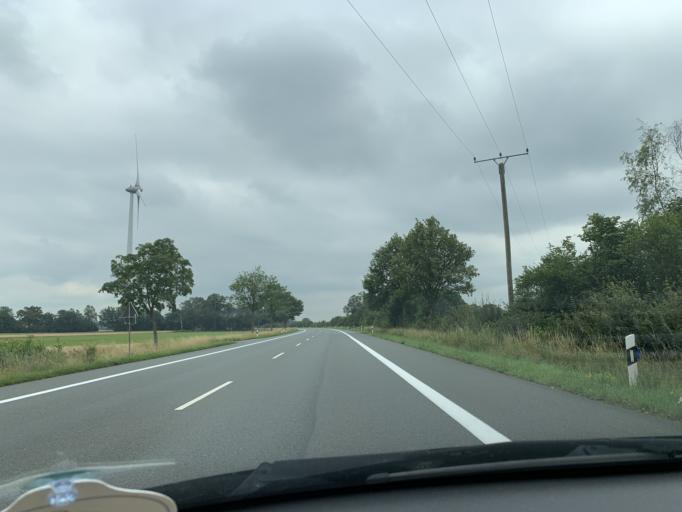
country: DE
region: North Rhine-Westphalia
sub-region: Regierungsbezirk Munster
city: Warendorf
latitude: 51.9333
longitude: 8.0215
